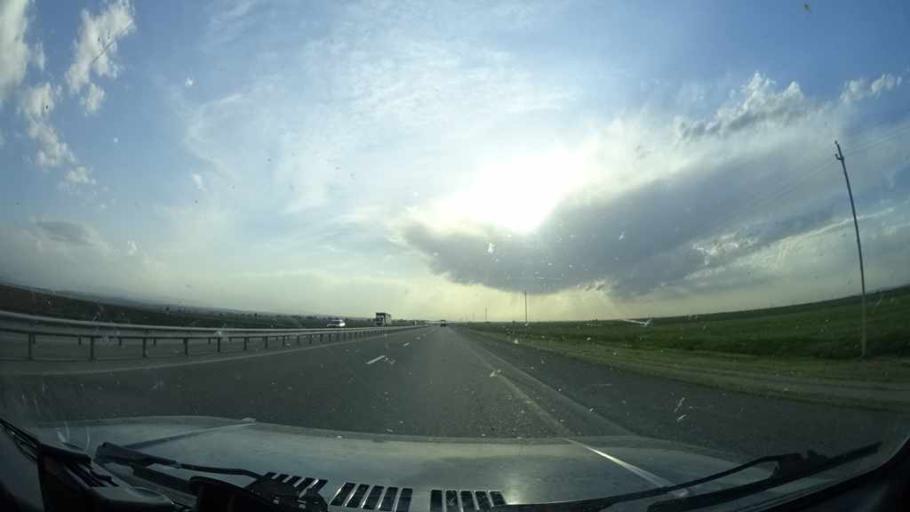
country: AZ
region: Goranboy
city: Goranboy
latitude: 40.6447
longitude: 46.7209
